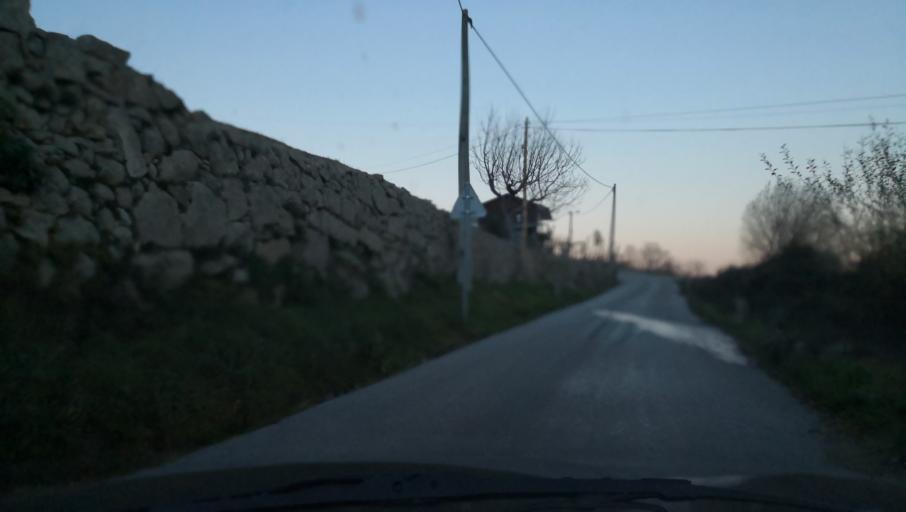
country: PT
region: Vila Real
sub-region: Vila Real
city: Vila Real
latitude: 41.3181
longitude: -7.7873
